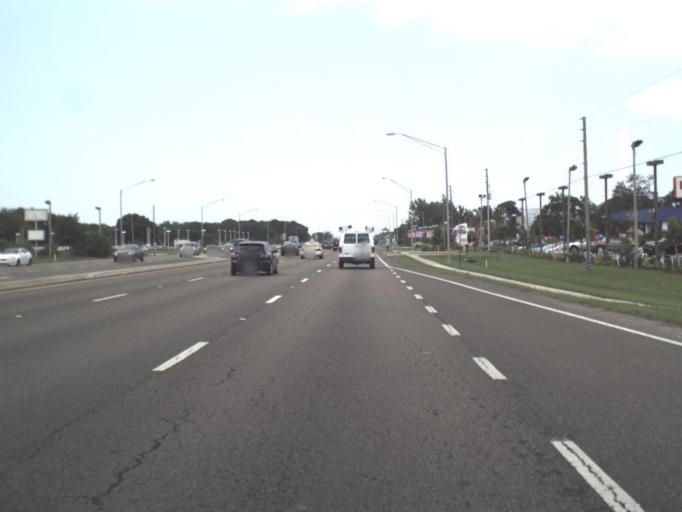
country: US
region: Florida
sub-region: Pinellas County
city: Pinellas Park
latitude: 27.8470
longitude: -82.6891
